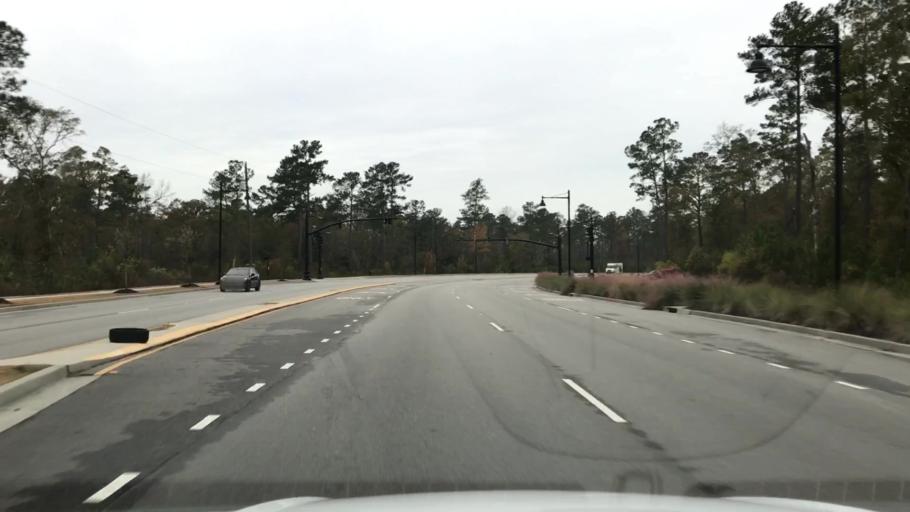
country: US
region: South Carolina
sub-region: Berkeley County
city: Ladson
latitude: 32.9592
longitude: -80.0760
